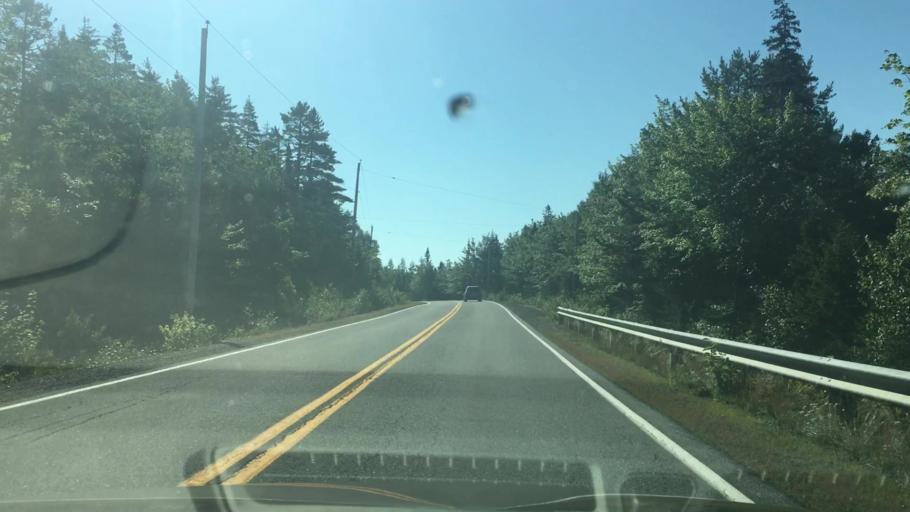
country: CA
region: Nova Scotia
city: Cole Harbour
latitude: 44.8092
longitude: -62.8348
